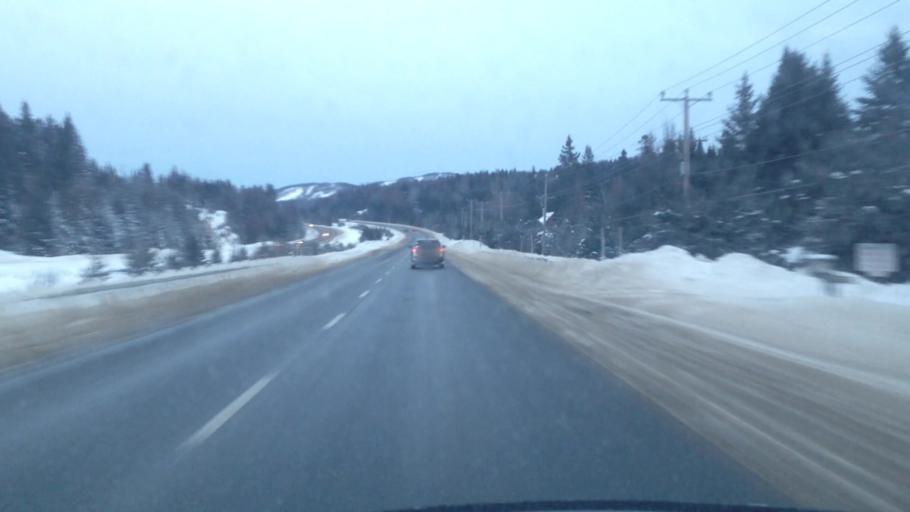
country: CA
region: Quebec
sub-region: Laurentides
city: Mont-Tremblant
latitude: 46.1144
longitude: -74.5457
